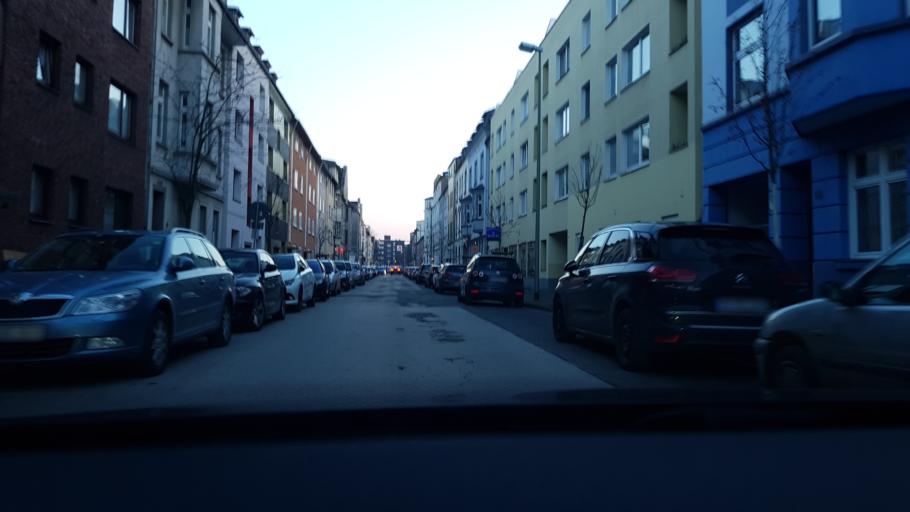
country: DE
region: North Rhine-Westphalia
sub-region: Regierungsbezirk Dusseldorf
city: Duisburg
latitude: 51.4363
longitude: 6.7885
